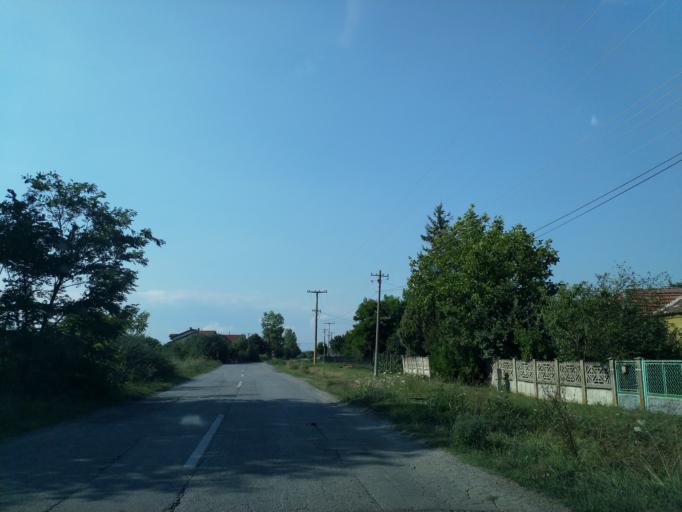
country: RS
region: Central Serbia
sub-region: Rasinski Okrug
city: Cicevac
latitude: 43.7685
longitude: 21.4278
